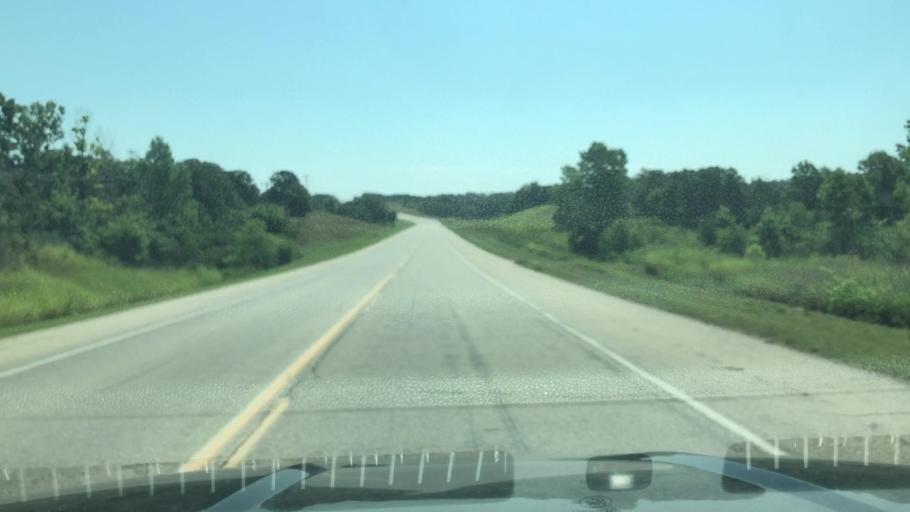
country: US
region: Oklahoma
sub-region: Creek County
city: Mannford
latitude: 36.0030
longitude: -96.4011
